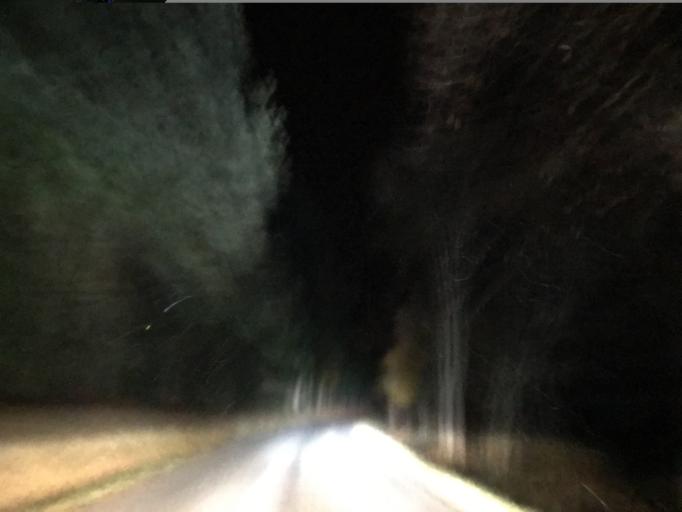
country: FR
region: Auvergne
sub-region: Departement du Puy-de-Dome
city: Saint-Remy-sur-Durolle
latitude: 45.9001
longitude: 3.6313
